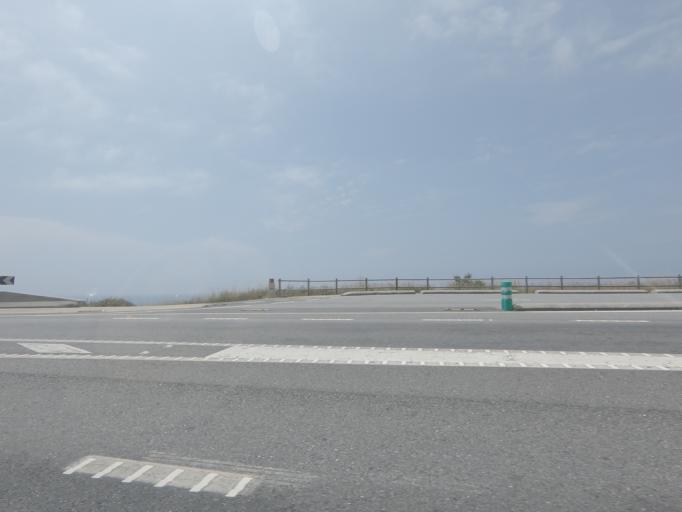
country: ES
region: Galicia
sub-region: Provincia de Pontevedra
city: A Guarda
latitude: 41.9373
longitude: -8.8849
